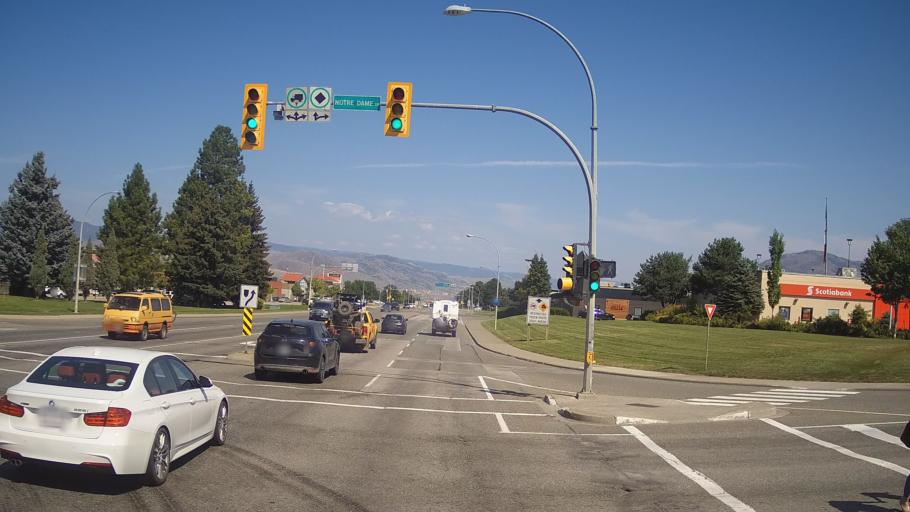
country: CA
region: British Columbia
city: Kamloops
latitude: 50.6637
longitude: -120.3537
